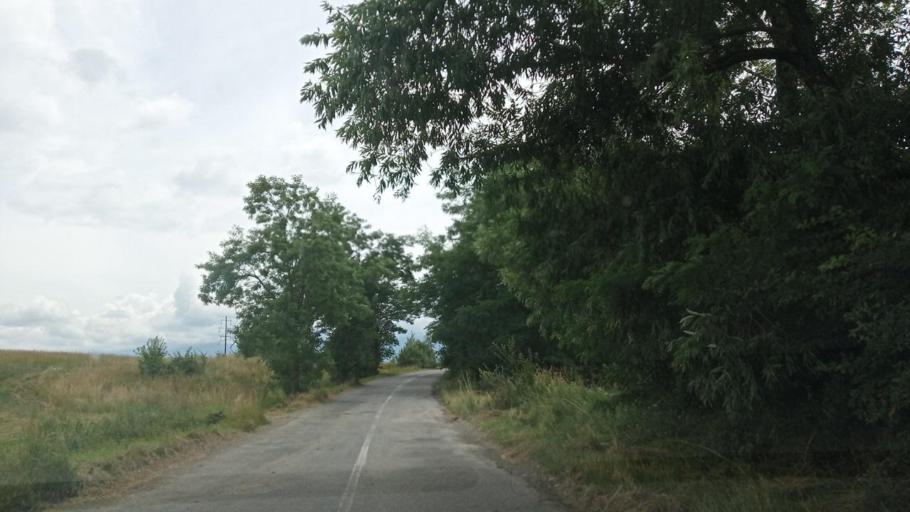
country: RO
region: Sibiu
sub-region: Comuna Porumbacu de Jos
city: Porumbacu de Jos
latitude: 45.7493
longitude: 24.4618
